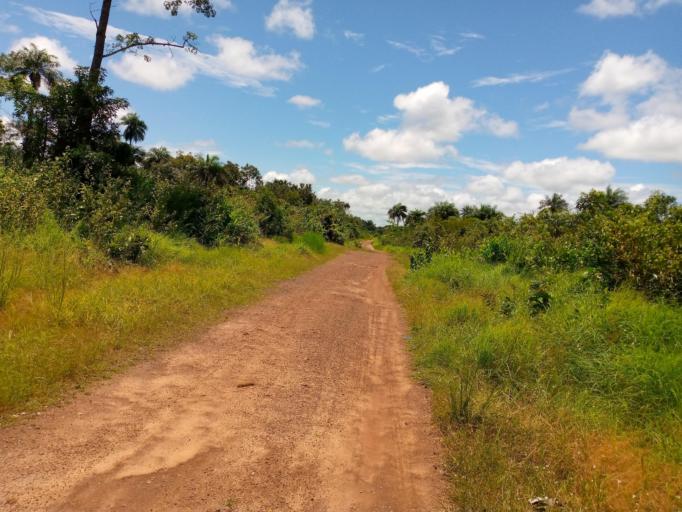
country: SL
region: Northern Province
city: Binkolo
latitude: 9.0650
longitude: -12.1493
